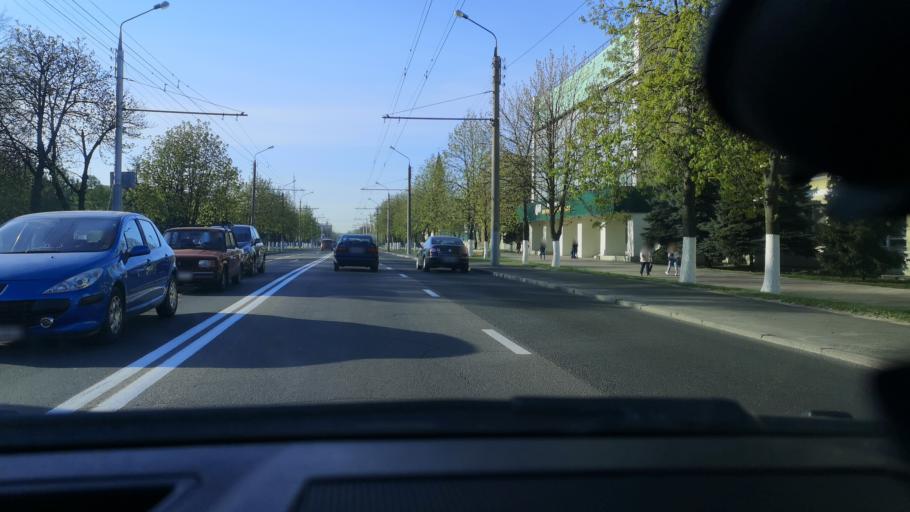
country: BY
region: Gomel
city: Gomel
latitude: 52.4497
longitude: 30.9965
